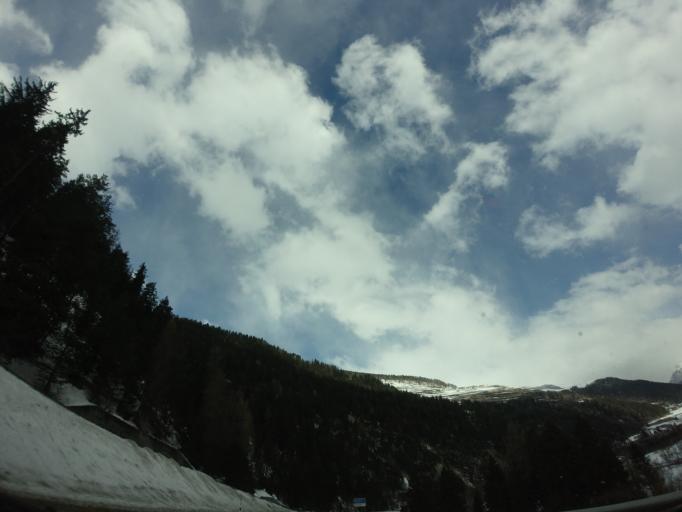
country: AT
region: Tyrol
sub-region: Politischer Bezirk Landeck
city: Nauders
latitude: 46.8541
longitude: 10.4216
